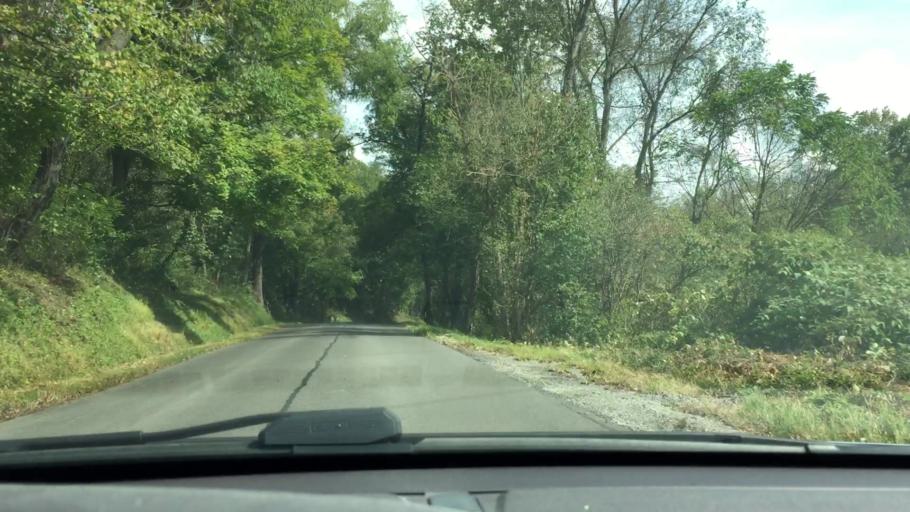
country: US
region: Pennsylvania
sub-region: Washington County
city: Thompsonville
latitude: 40.2931
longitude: -80.1375
